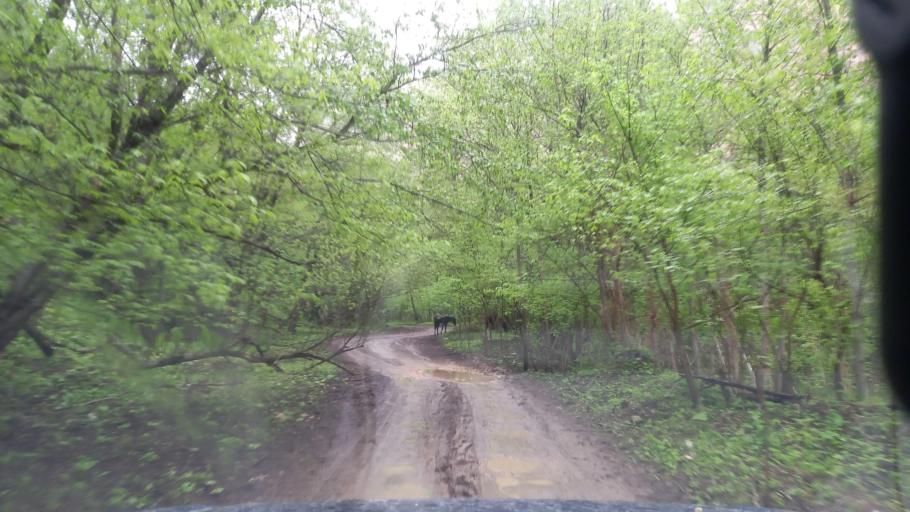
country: RU
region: Kabardino-Balkariya
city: Bylym
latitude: 43.5910
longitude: 42.9885
